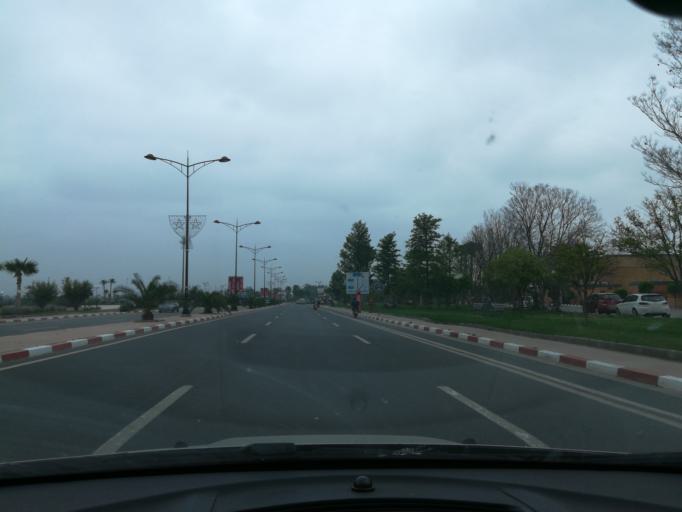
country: MA
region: Marrakech-Tensift-Al Haouz
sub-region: Marrakech
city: Marrakesh
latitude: 31.6841
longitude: -7.9939
